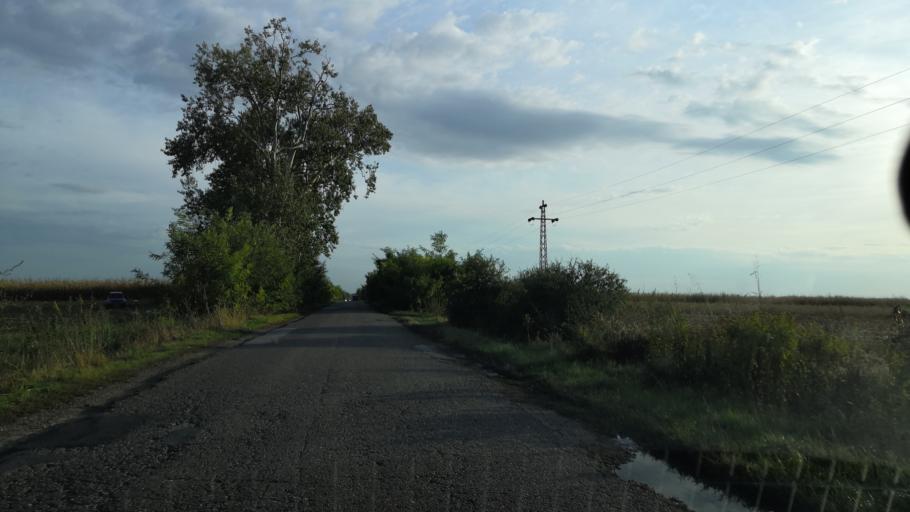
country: RS
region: Autonomna Pokrajina Vojvodina
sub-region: Sremski Okrug
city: Stara Pazova
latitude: 45.0149
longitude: 20.1684
